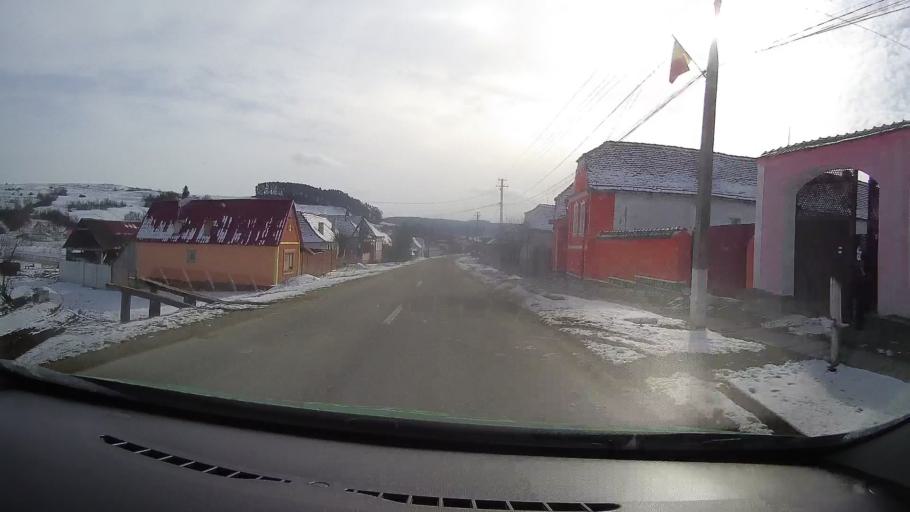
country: RO
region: Sibiu
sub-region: Comuna Bradeni
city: Bradeni
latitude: 46.0872
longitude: 24.8328
